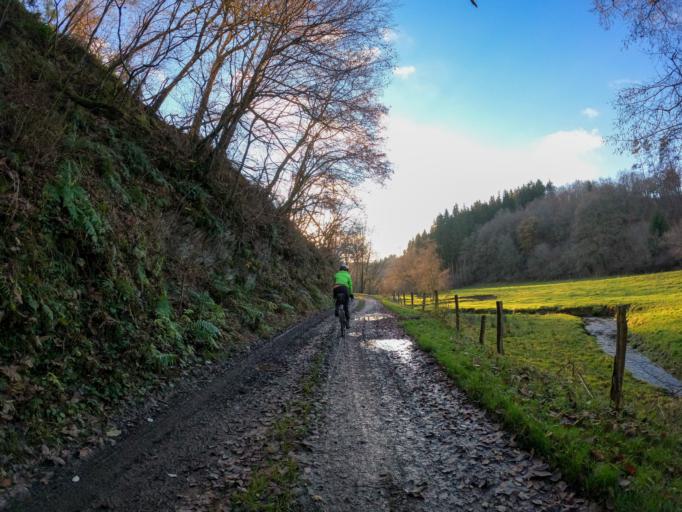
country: LU
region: Diekirch
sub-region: Canton de Wiltz
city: Bavigne
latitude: 49.9484
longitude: 5.8393
